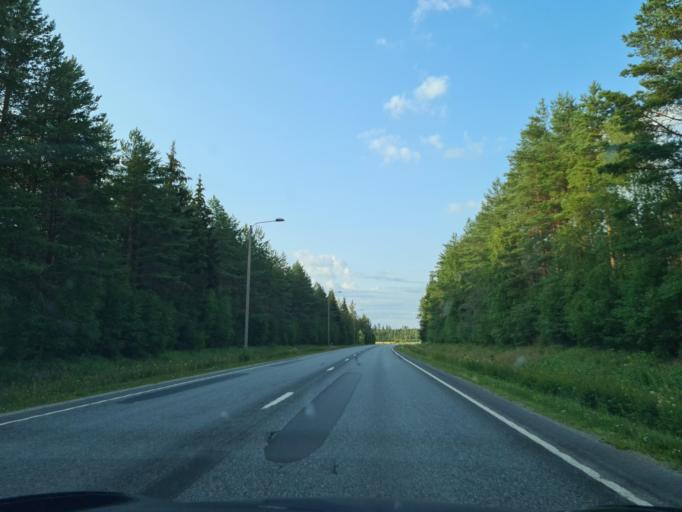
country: FI
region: Southern Ostrobothnia
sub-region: Seinaejoki
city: Kauhava
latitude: 63.0654
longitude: 23.0442
